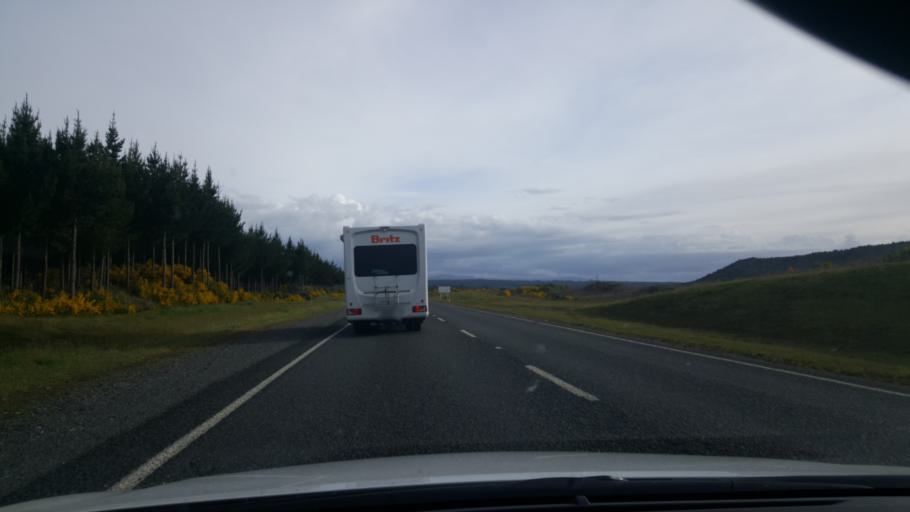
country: NZ
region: Waikato
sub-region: Taupo District
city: Taupo
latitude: -38.8326
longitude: 176.0655
